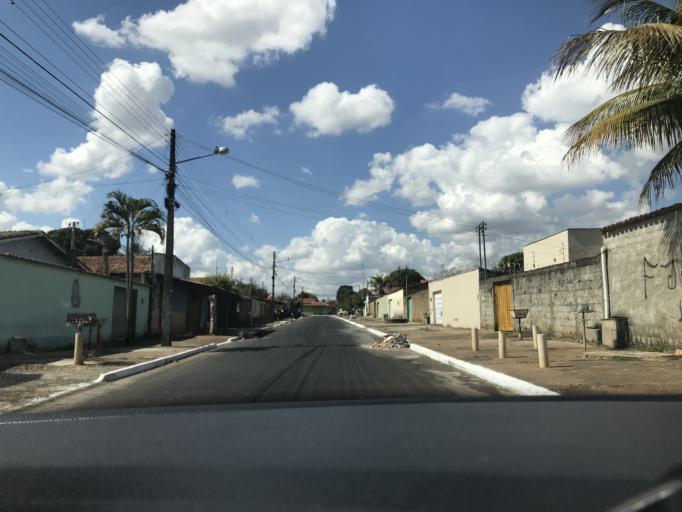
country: BR
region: Goias
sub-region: Senador Canedo
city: Senador Canedo
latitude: -16.6516
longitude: -49.1544
